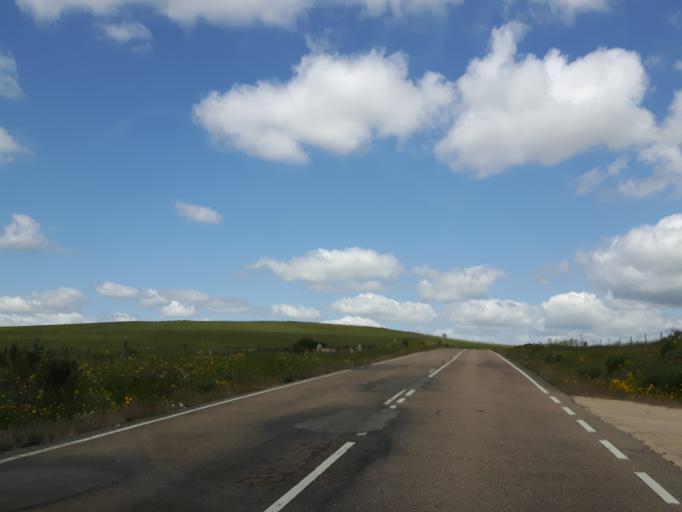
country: ES
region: Castille and Leon
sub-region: Provincia de Salamanca
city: Villar de la Yegua
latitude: 40.7175
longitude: -6.6951
